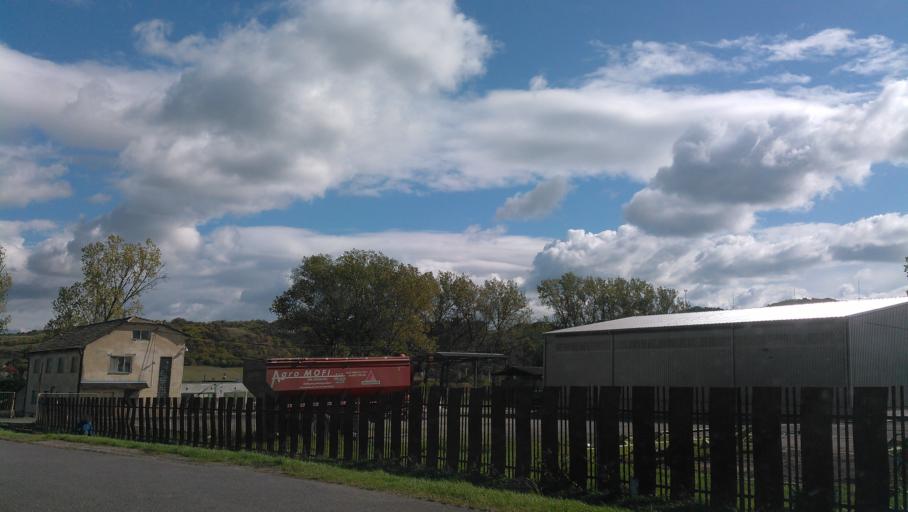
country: SK
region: Banskobystricky
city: Poltar
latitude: 48.3760
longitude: 19.8817
